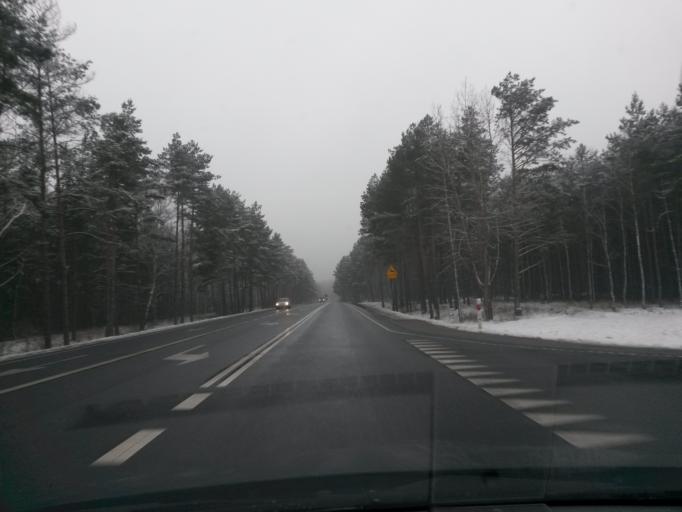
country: PL
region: Kujawsko-Pomorskie
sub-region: Powiat bydgoski
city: Nowa Wies Wielka
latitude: 53.0601
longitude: 18.0821
